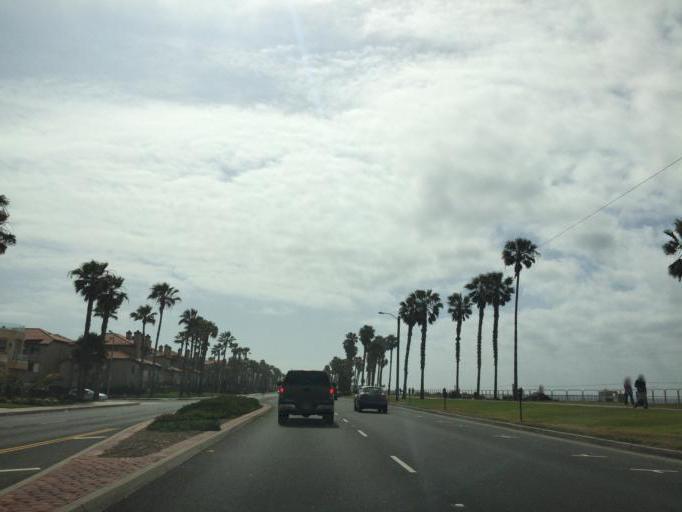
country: US
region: California
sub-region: Orange County
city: Huntington Beach
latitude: 33.6641
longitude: -118.0116
